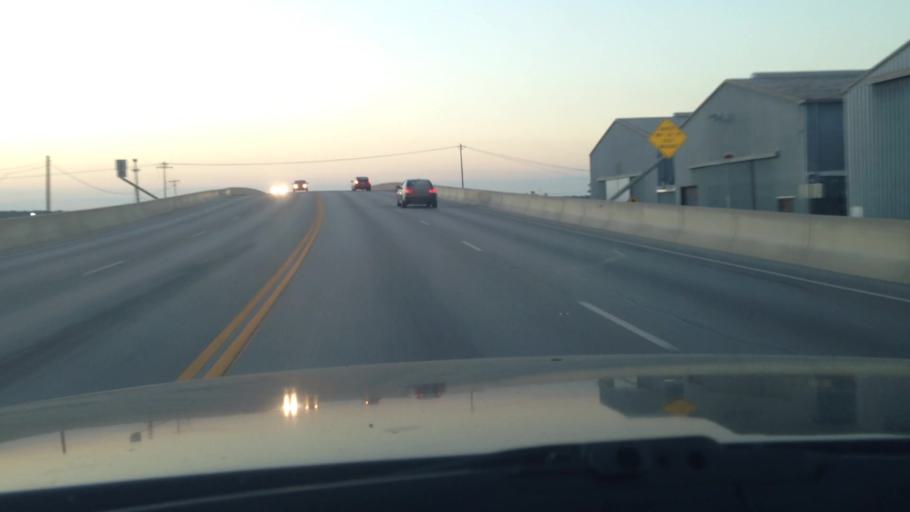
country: US
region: Texas
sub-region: Hays County
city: San Marcos
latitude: 29.8583
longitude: -97.9545
